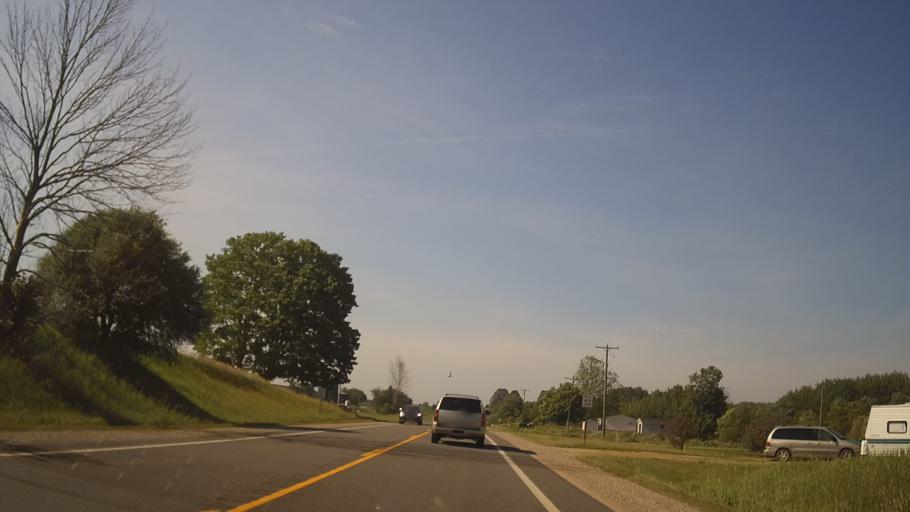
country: US
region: Michigan
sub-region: Ogemaw County
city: West Branch
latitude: 44.3770
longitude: -84.1159
